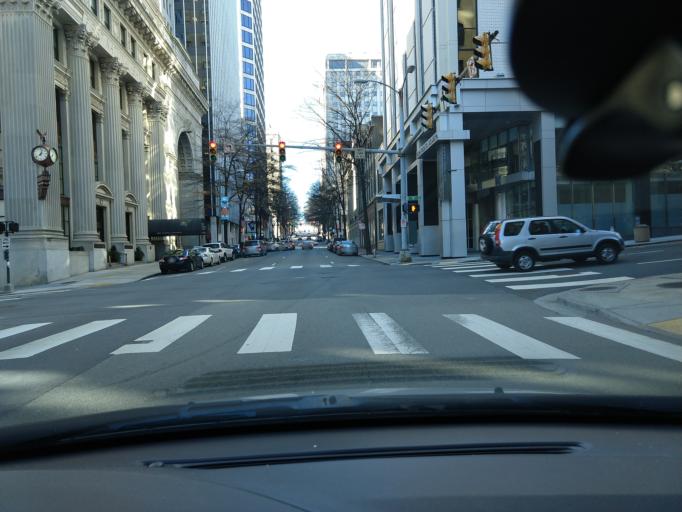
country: US
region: Virginia
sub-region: City of Richmond
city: Richmond
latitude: 37.5382
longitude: -77.4361
